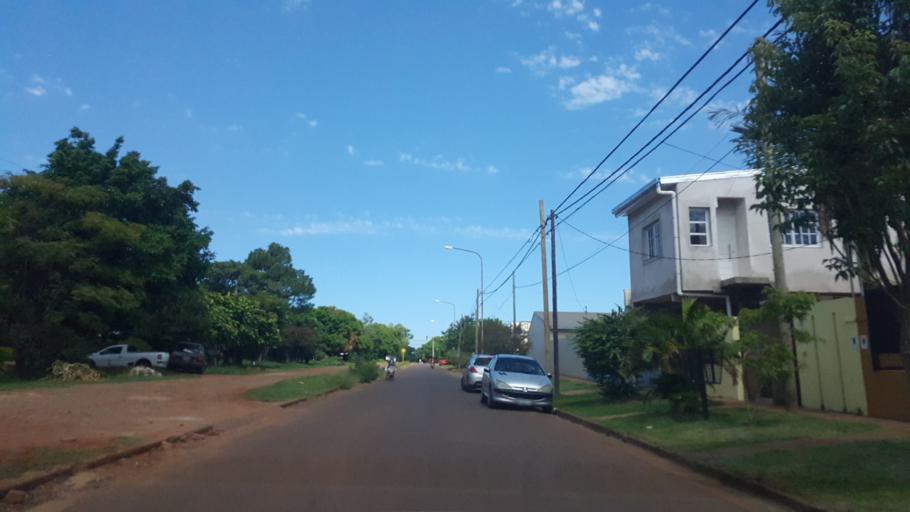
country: AR
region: Misiones
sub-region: Departamento de Capital
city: Posadas
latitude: -27.3836
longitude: -55.9227
